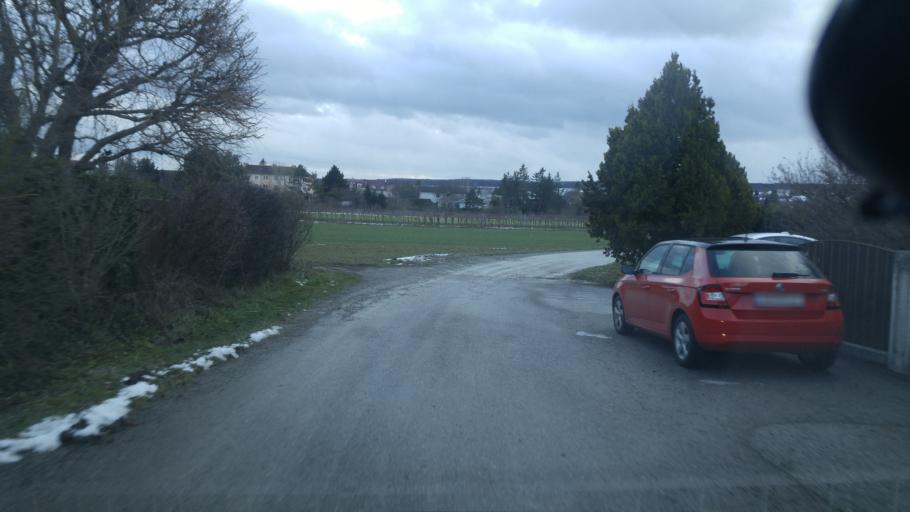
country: AT
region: Lower Austria
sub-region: Politischer Bezirk Baden
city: Bad Voslau
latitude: 47.9618
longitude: 16.1893
